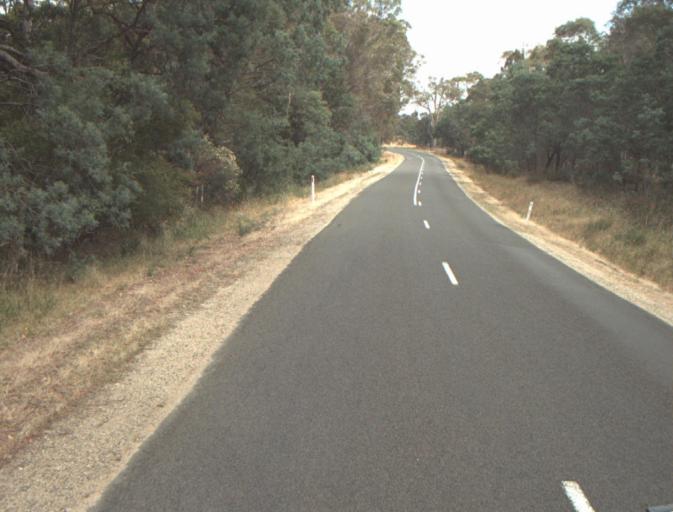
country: AU
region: Tasmania
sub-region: Northern Midlands
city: Evandale
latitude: -41.5078
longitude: 147.3222
